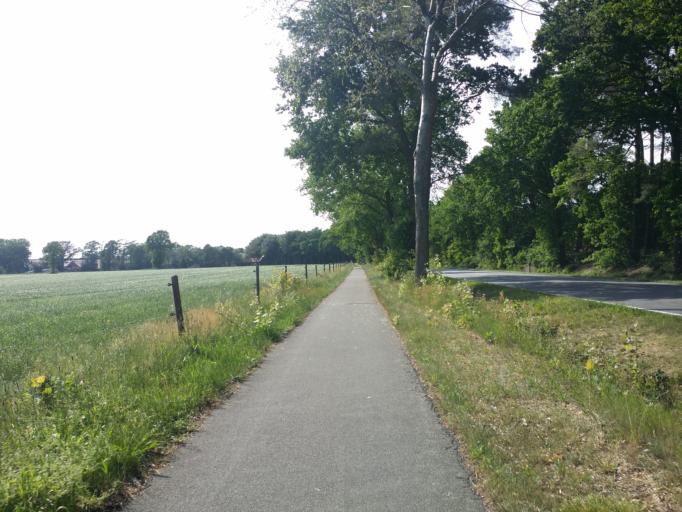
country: DE
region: Lower Saxony
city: Wiefelstede
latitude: 53.2873
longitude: 8.0876
